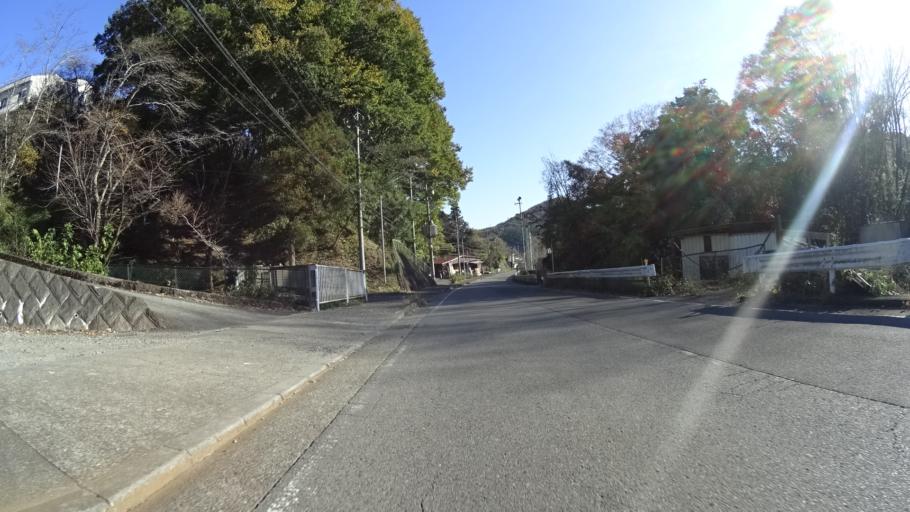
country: JP
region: Yamanashi
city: Uenohara
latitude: 35.6470
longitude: 139.1242
